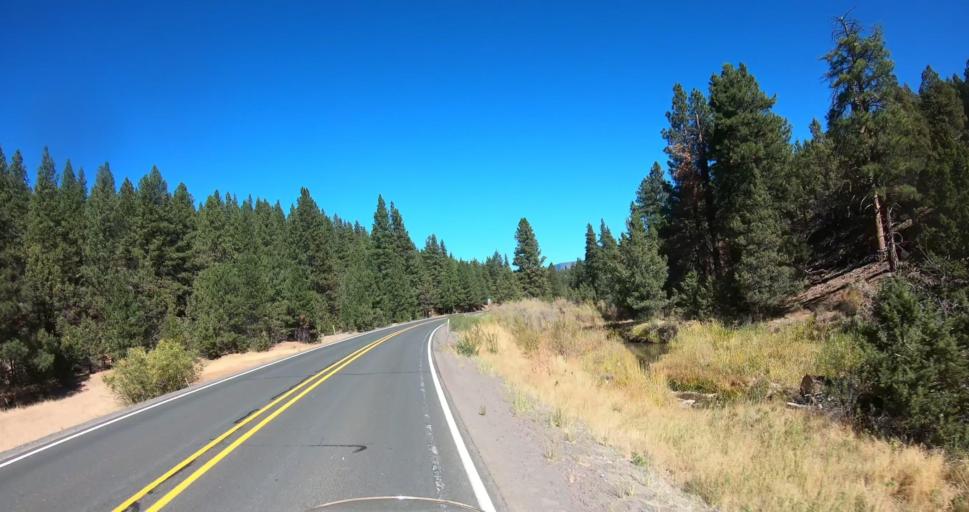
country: US
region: Oregon
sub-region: Lake County
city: Lakeview
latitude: 42.4026
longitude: -120.2927
